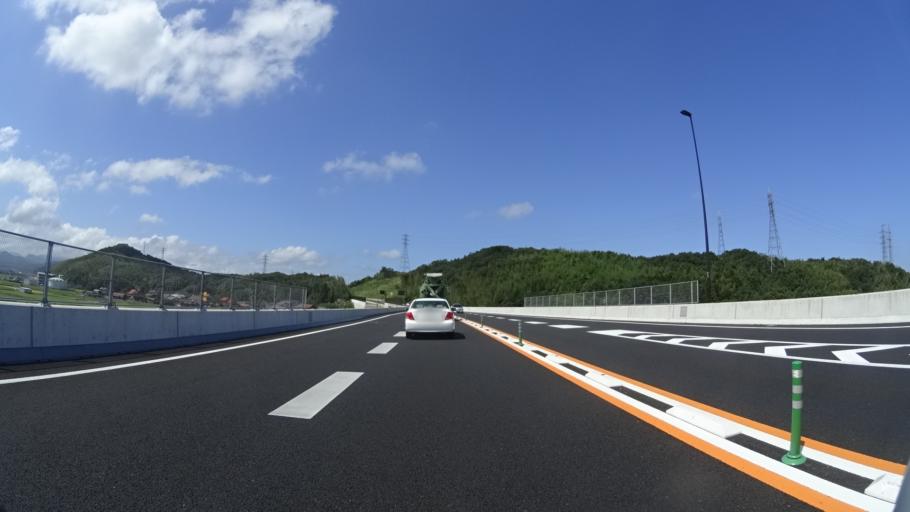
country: JP
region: Tottori
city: Tottori
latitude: 35.4947
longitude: 134.1881
